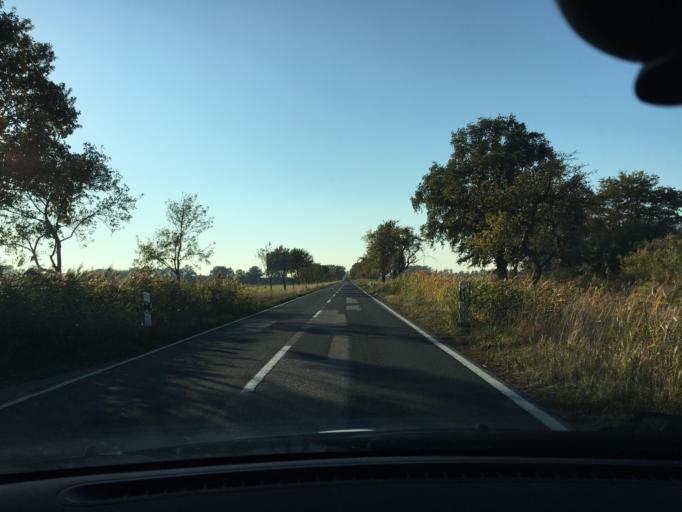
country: DE
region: Lower Saxony
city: Neu Darchau
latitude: 53.2877
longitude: 10.8459
